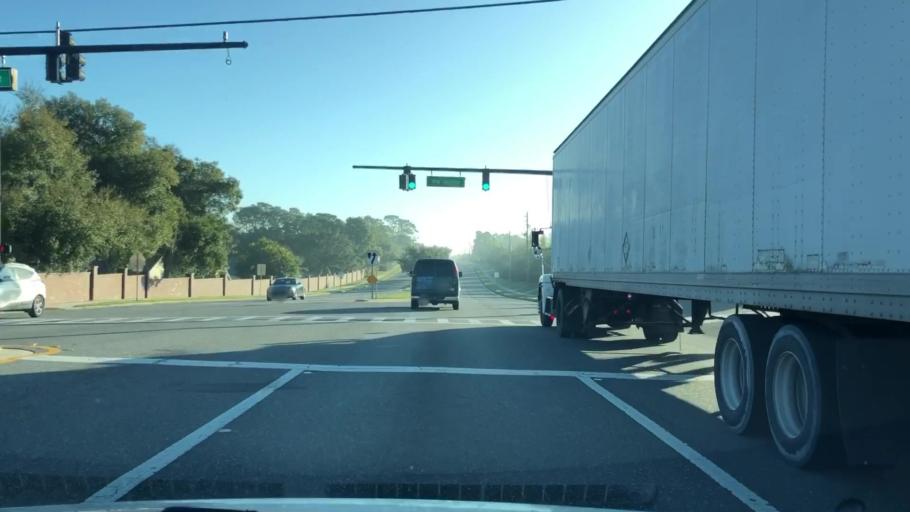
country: US
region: Florida
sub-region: Seminole County
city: Lake Mary
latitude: 28.7864
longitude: -81.3290
